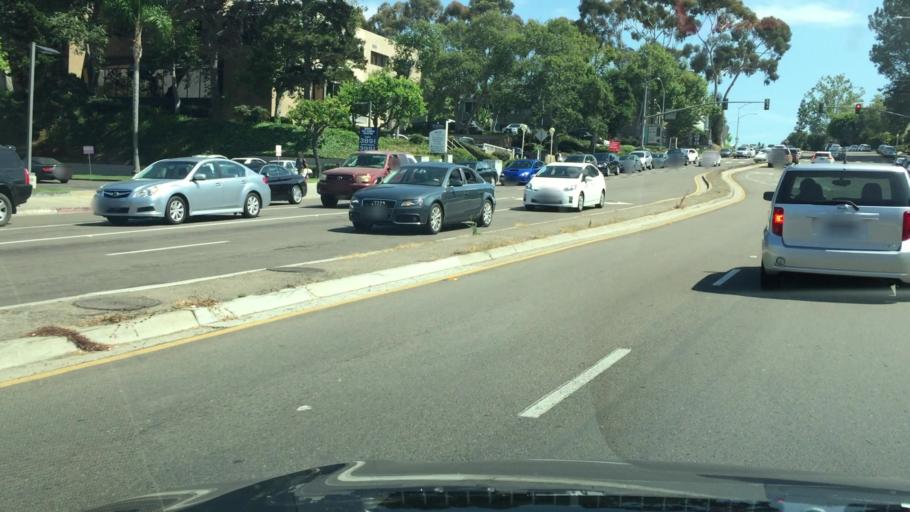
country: US
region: California
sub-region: San Diego County
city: La Jolla
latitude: 32.8714
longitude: -117.2340
